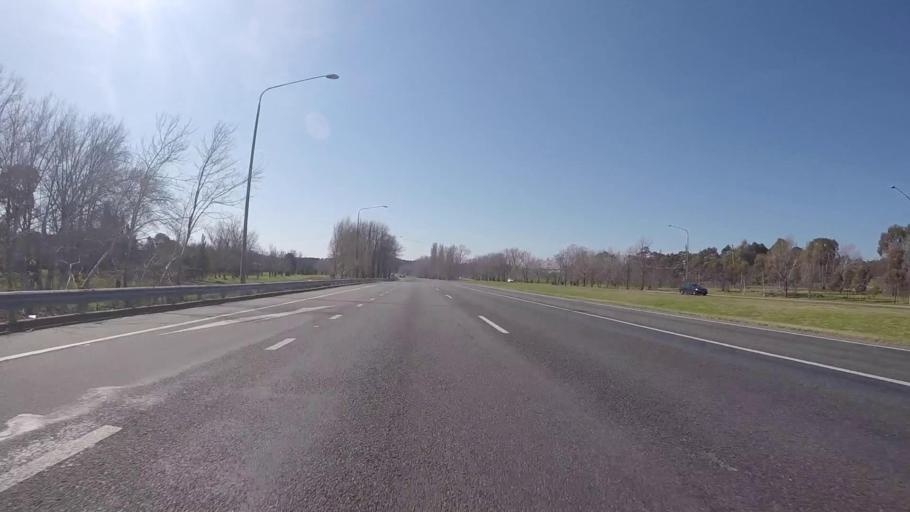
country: AU
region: Australian Capital Territory
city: Forrest
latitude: -35.3241
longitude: 149.0878
